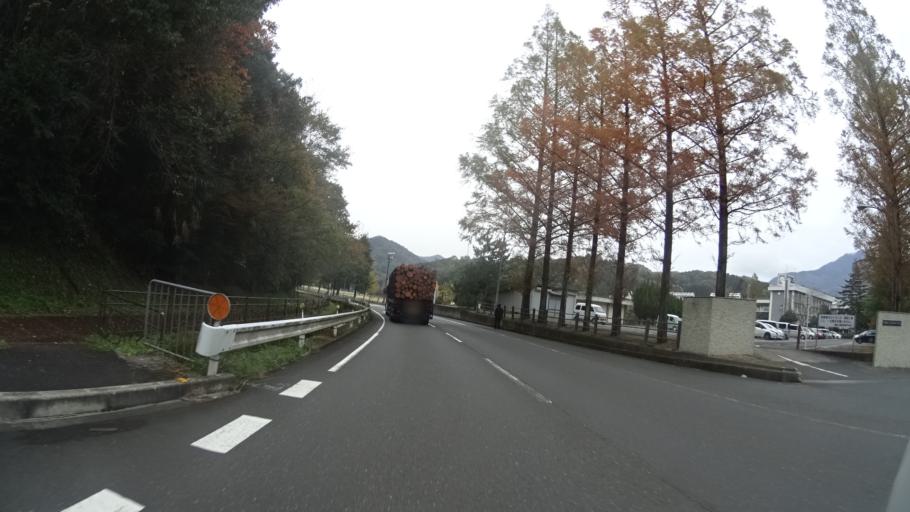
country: JP
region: Kyoto
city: Maizuru
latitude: 35.4948
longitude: 135.4381
